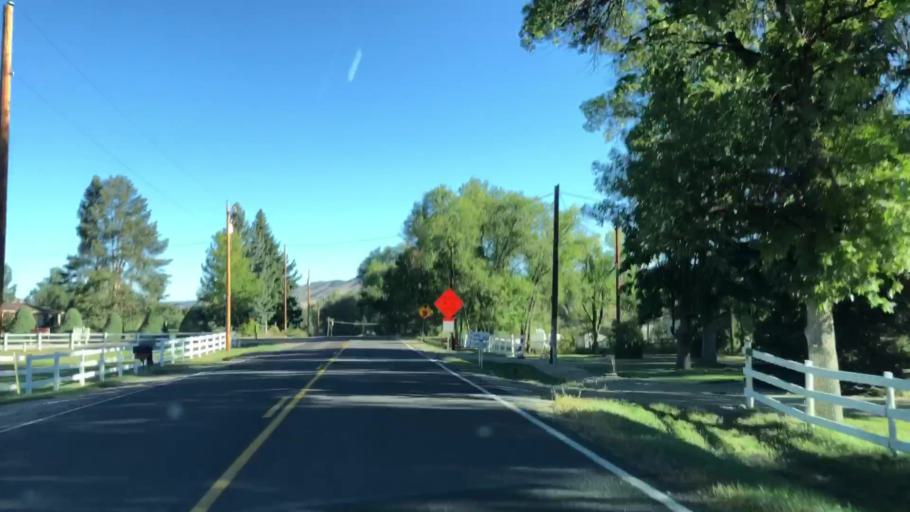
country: US
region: Colorado
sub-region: Larimer County
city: Loveland
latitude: 40.4107
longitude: -105.1688
